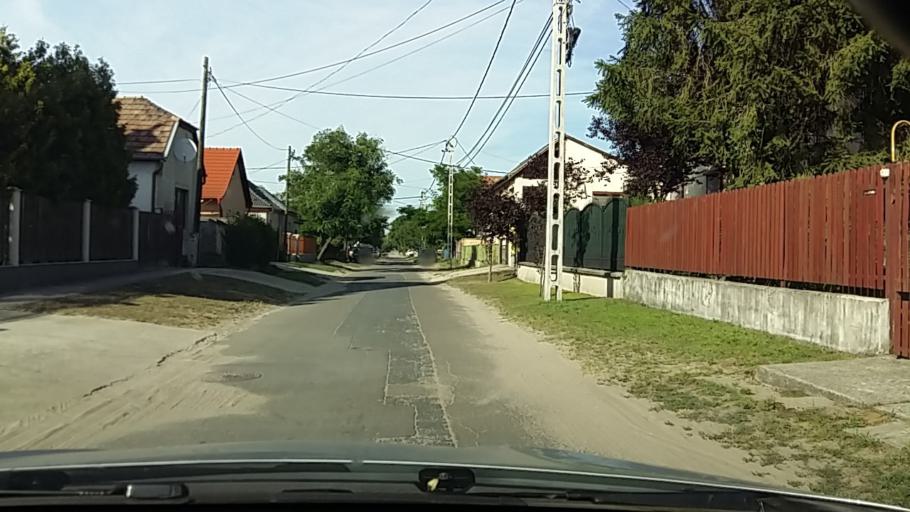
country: HU
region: Pest
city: God
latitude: 47.6989
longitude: 19.1495
